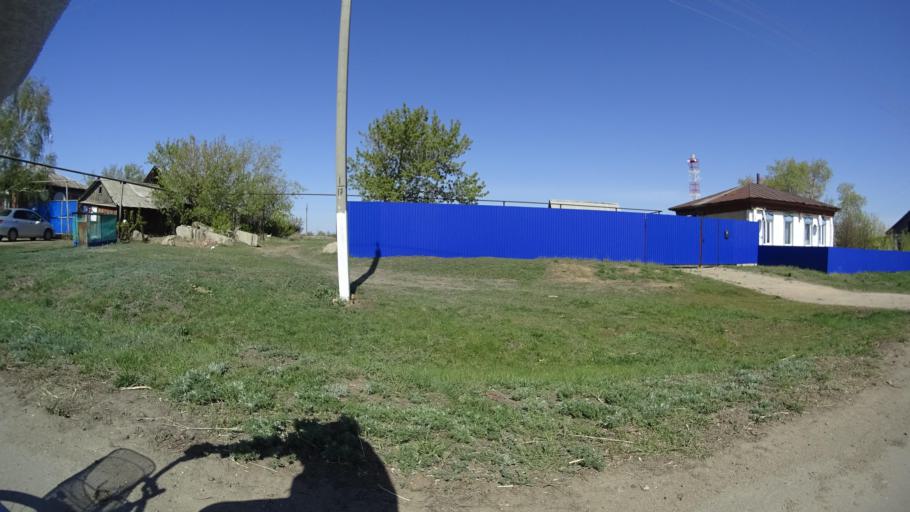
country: RU
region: Chelyabinsk
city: Chesma
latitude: 53.7926
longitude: 61.0369
